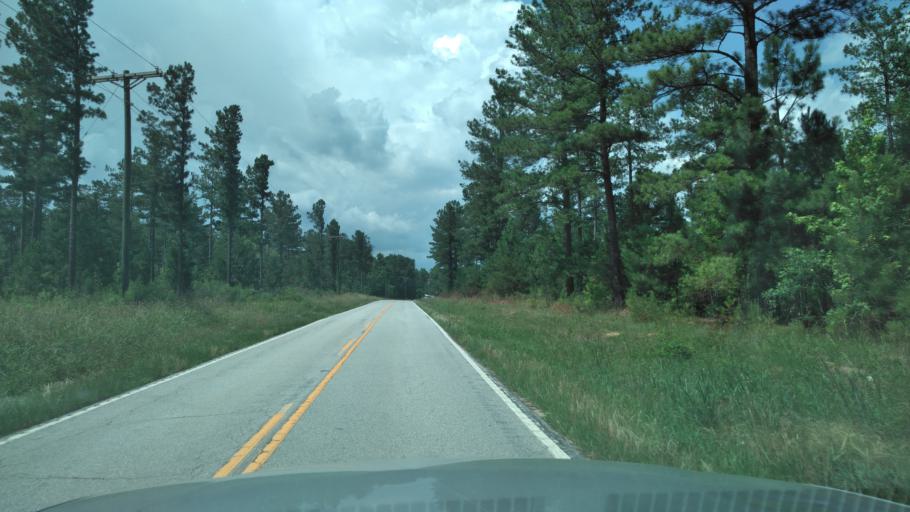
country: US
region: South Carolina
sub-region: Laurens County
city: Laurens
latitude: 34.5245
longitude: -82.0933
